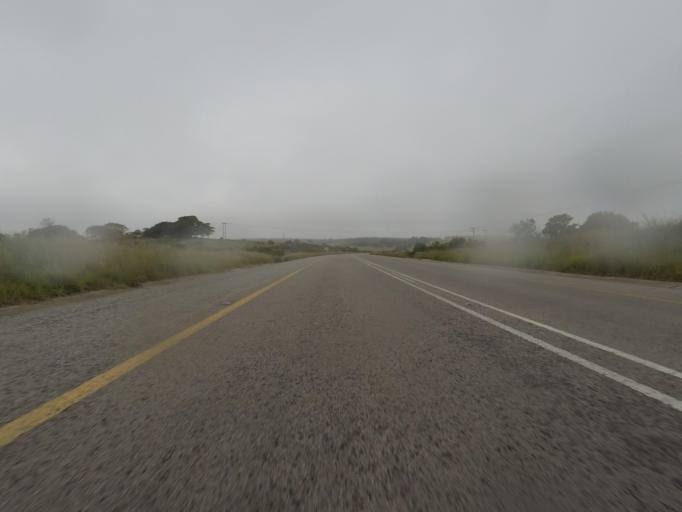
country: ZA
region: Eastern Cape
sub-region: Cacadu District Municipality
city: Grahamstown
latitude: -33.6425
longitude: 26.3713
